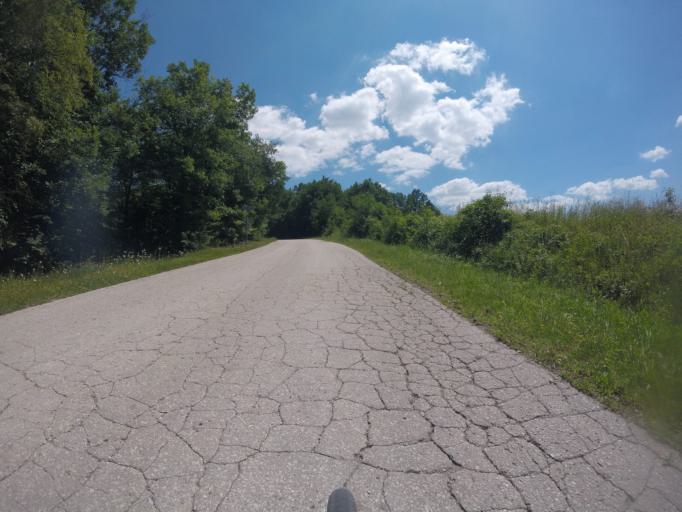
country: HR
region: Karlovacka
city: Ozalj
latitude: 45.6671
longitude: 15.4270
